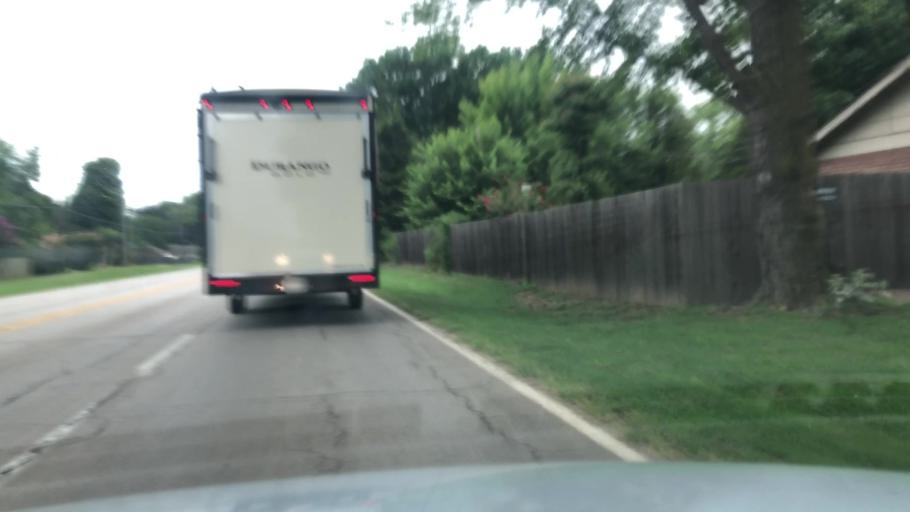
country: US
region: Oklahoma
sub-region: Washington County
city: Bartlesville
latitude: 36.7281
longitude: -95.9123
